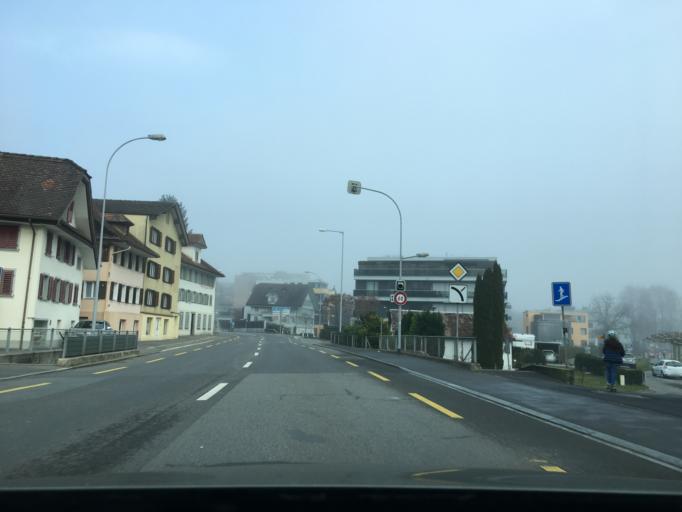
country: CH
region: Schwyz
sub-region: Bezirk Kuessnacht
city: Kussnacht
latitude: 47.0818
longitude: 8.4332
